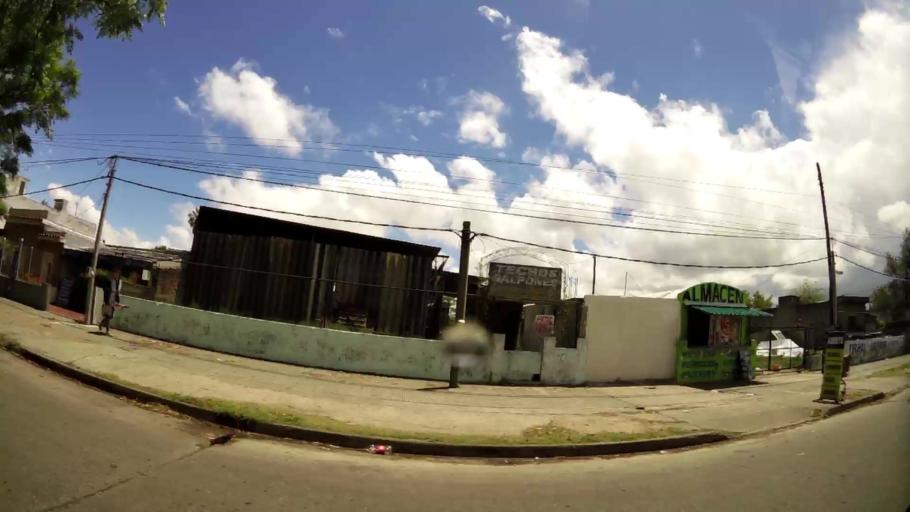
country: UY
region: Montevideo
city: Montevideo
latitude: -34.8513
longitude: -56.1801
